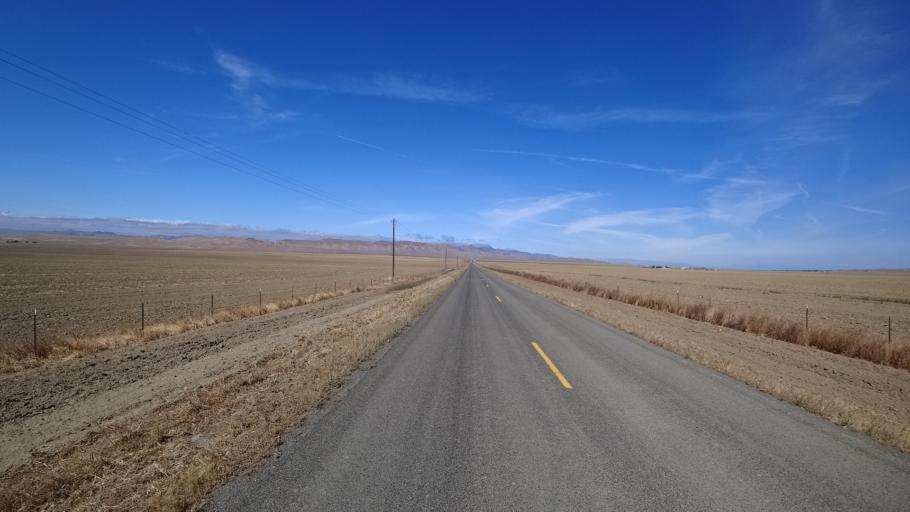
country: US
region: California
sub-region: Kings County
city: Kettleman City
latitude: 35.9351
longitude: -120.0430
